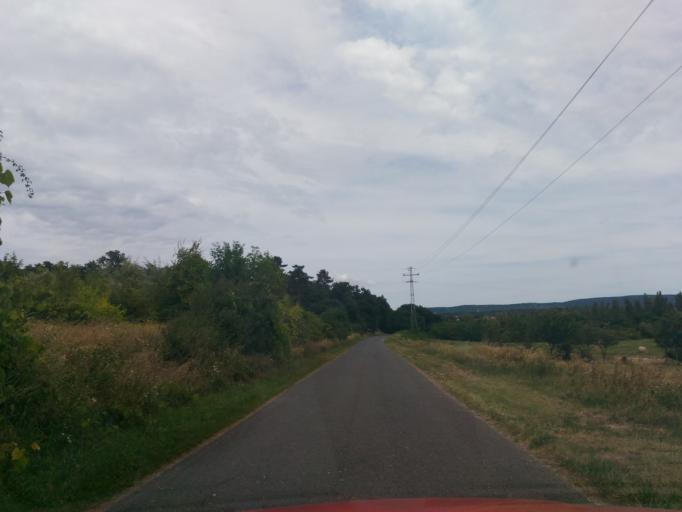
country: HU
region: Veszprem
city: Zanka
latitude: 46.8663
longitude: 17.6739
